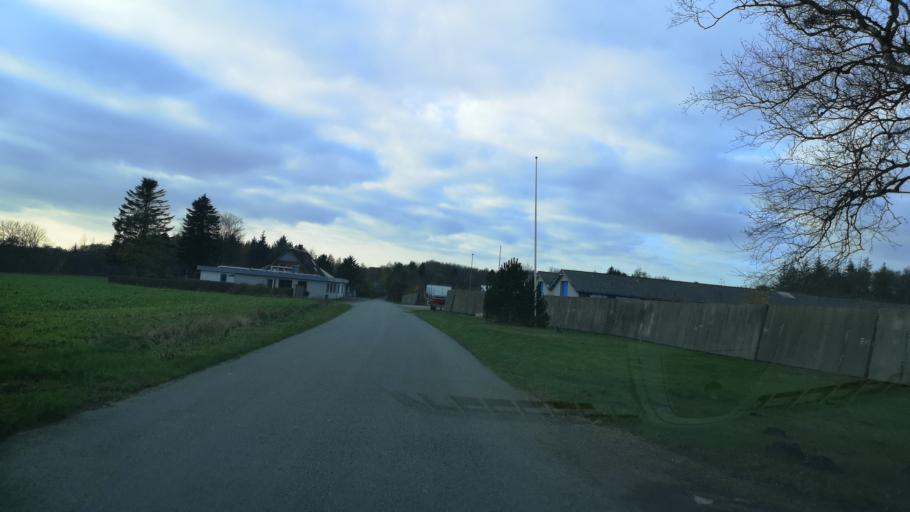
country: DK
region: Central Jutland
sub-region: Ringkobing-Skjern Kommune
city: Videbaek
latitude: 56.0402
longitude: 8.6052
